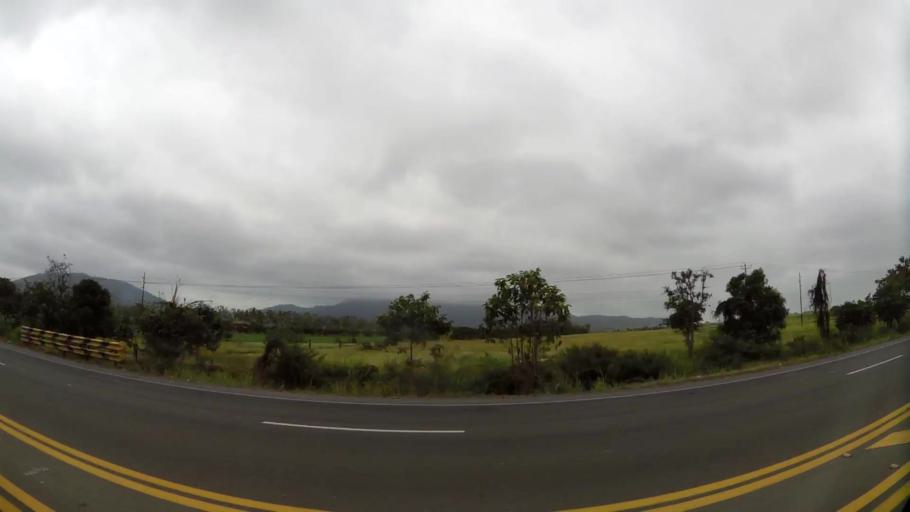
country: EC
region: Guayas
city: Naranjal
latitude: -2.4870
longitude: -79.6117
